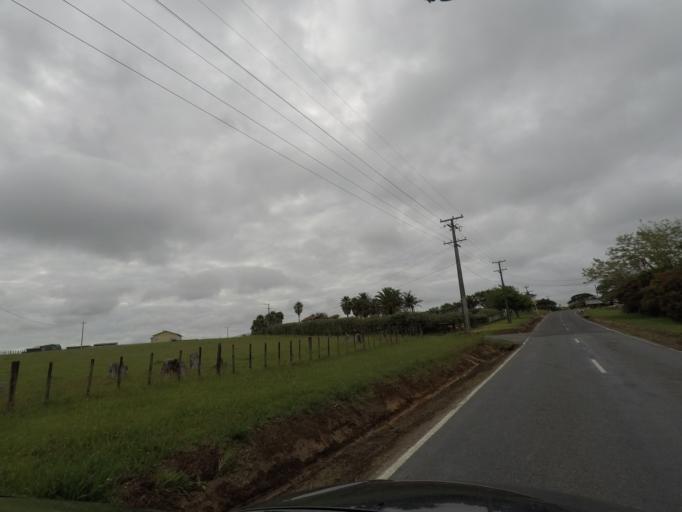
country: NZ
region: Auckland
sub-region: Auckland
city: Rosebank
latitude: -36.8098
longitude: 174.5772
